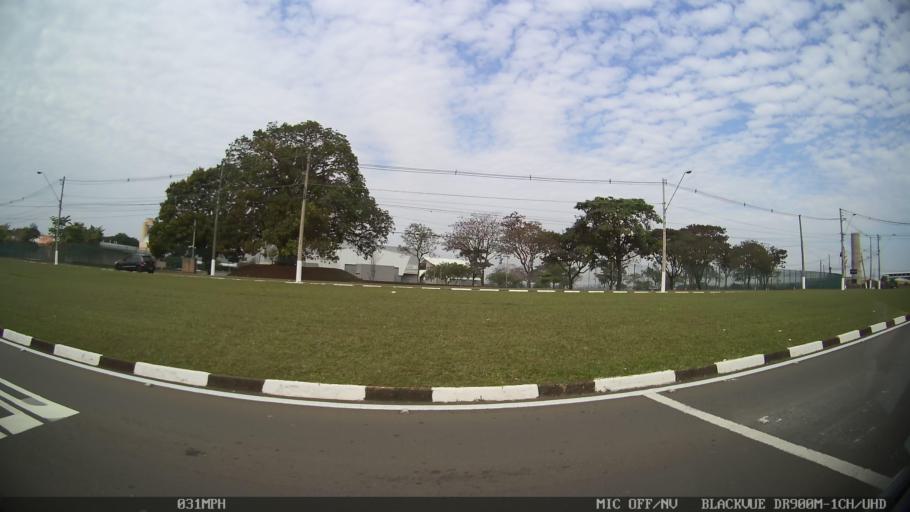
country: BR
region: Sao Paulo
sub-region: Paulinia
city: Paulinia
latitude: -22.7816
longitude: -47.1569
